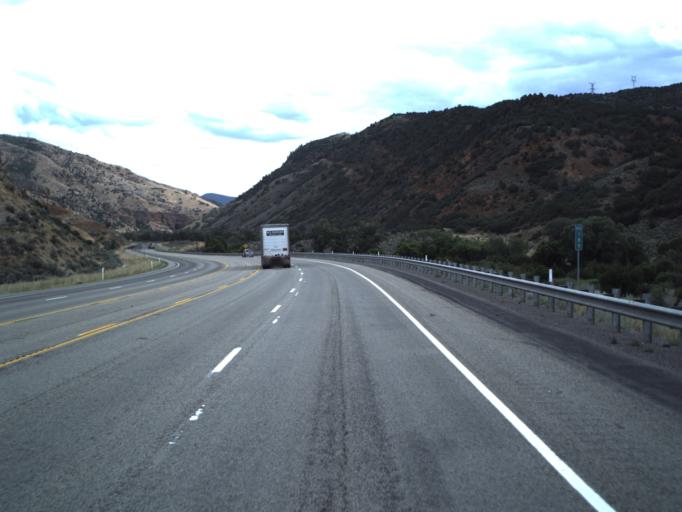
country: US
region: Utah
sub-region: Utah County
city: Mapleton
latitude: 39.9959
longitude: -111.4409
